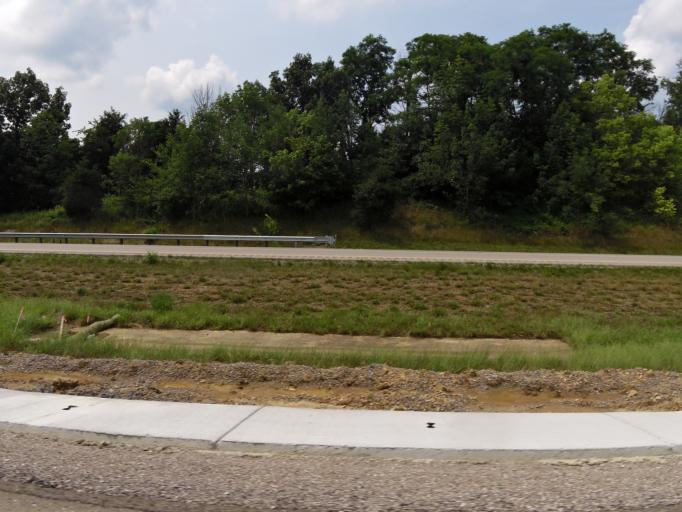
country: US
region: Kentucky
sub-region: Boone County
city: Verona
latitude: 38.8122
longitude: -84.7124
